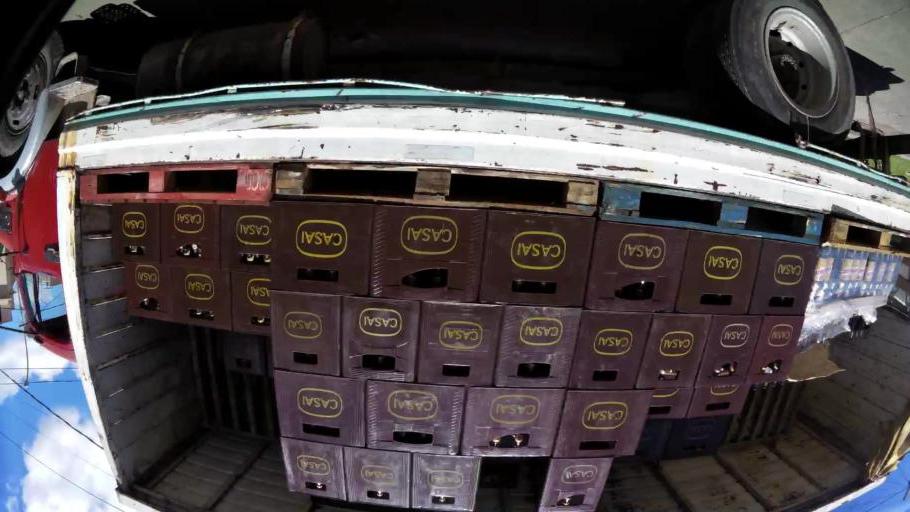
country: AR
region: Buenos Aires
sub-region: Partido de Lanus
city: Lanus
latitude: -34.6963
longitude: -58.4148
